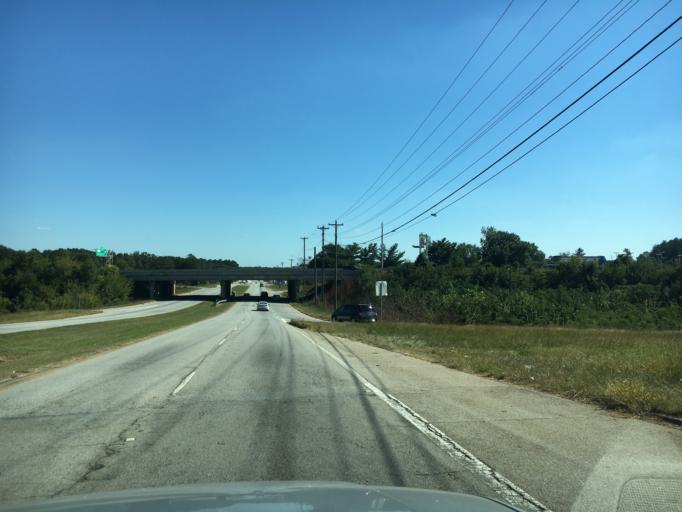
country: US
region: South Carolina
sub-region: Greenville County
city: Mauldin
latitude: 34.8147
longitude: -82.3379
